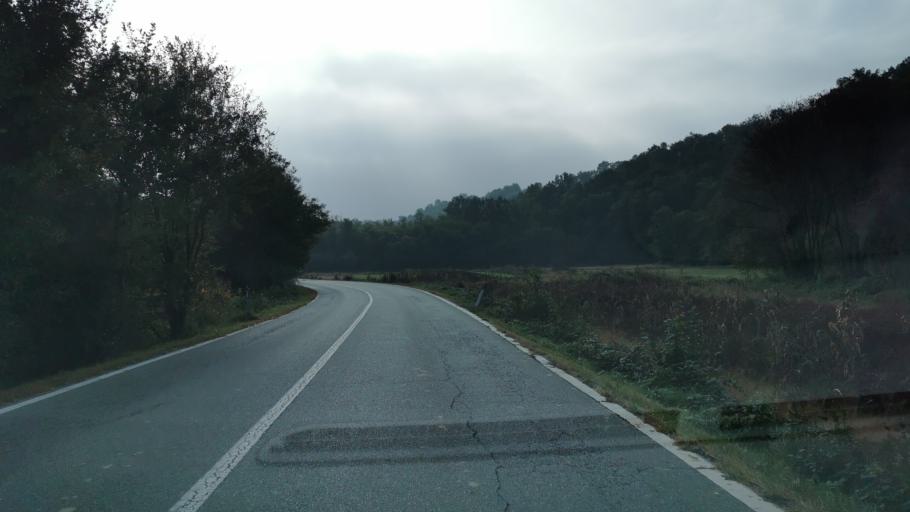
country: IT
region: Piedmont
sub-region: Provincia di Torino
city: Front
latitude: 45.2692
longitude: 7.6828
